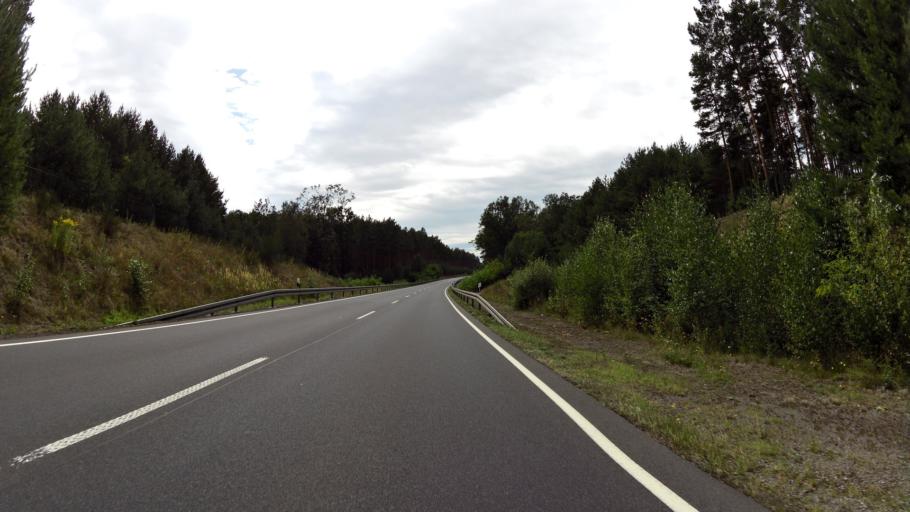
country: DE
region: Brandenburg
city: Schenkendobern
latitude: 51.9823
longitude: 14.6544
